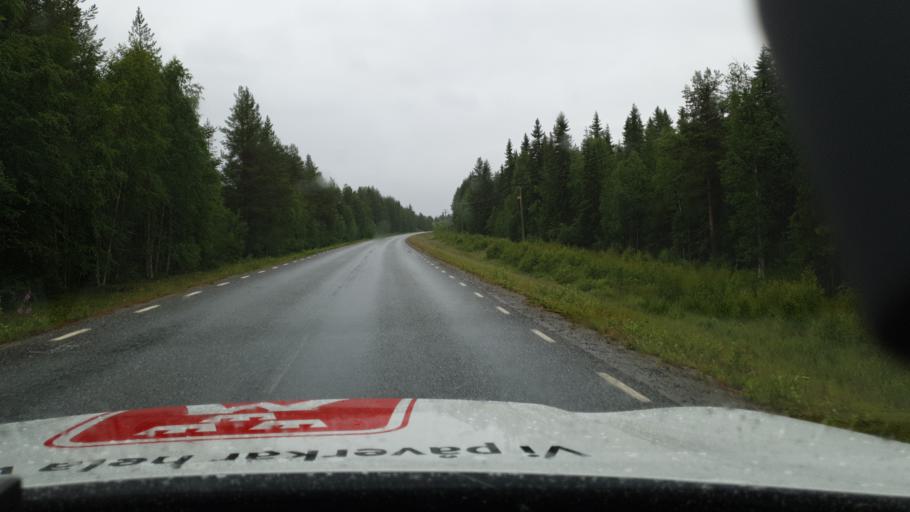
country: SE
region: Vaesterbotten
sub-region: Asele Kommun
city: Asele
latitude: 64.3407
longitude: 17.0252
